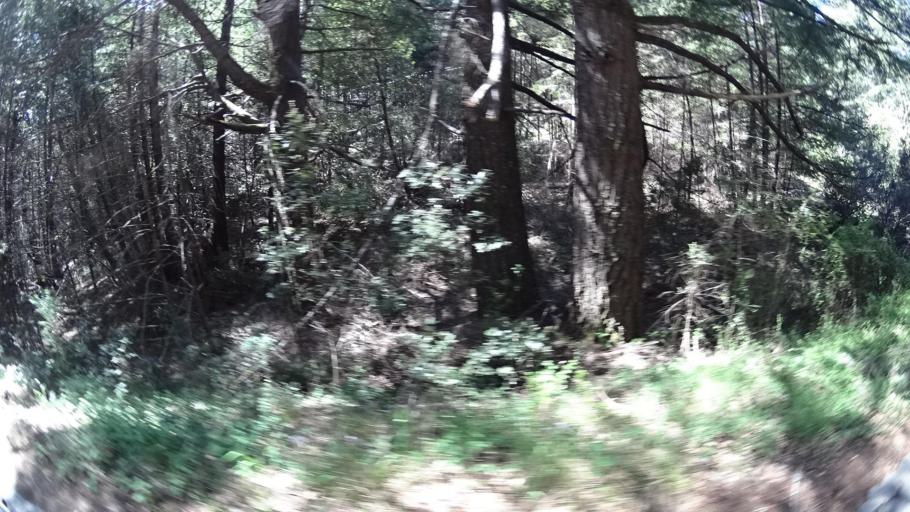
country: US
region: California
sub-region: Humboldt County
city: Redway
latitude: 40.1961
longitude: -124.0984
